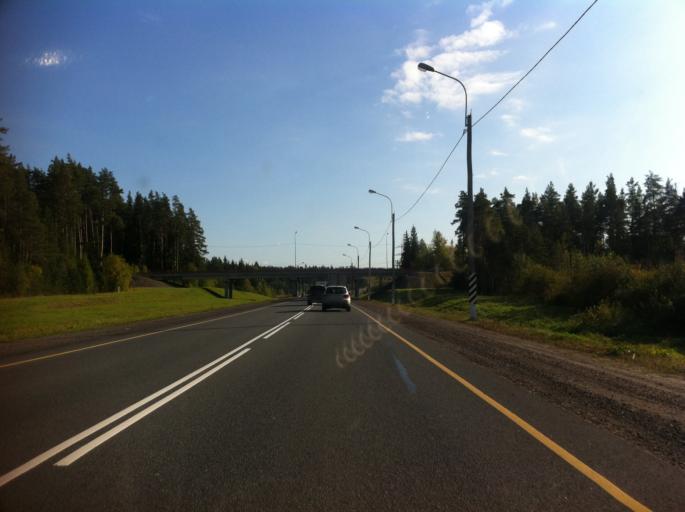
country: RU
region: Leningrad
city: Luga
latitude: 58.7592
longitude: 29.8859
